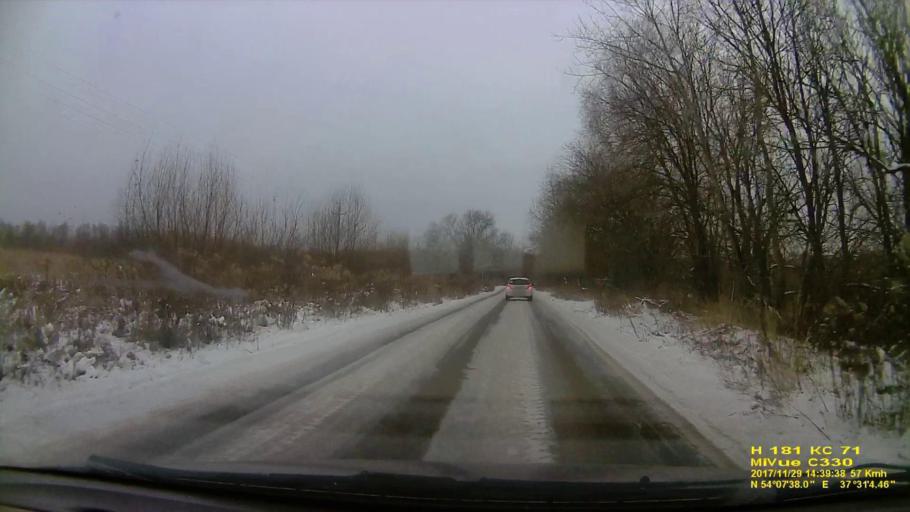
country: RU
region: Tula
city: Kosaya Gora
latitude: 54.1272
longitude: 37.5179
